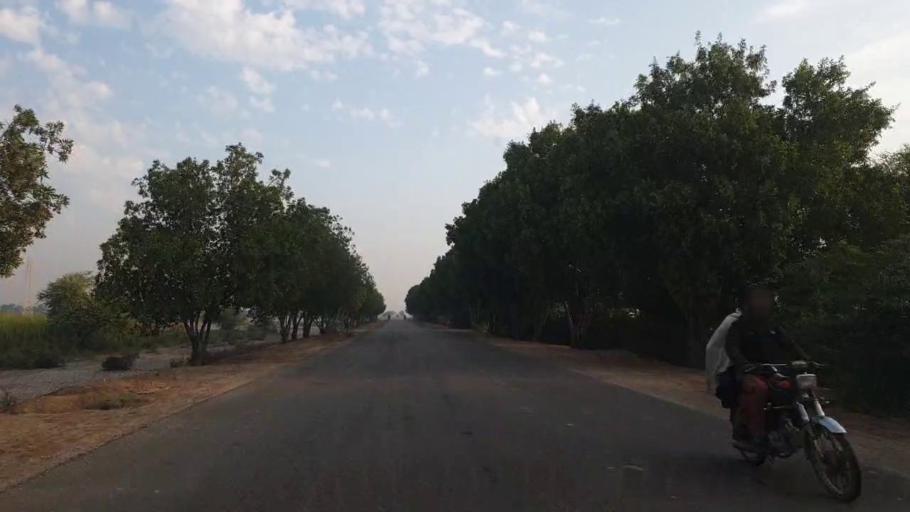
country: PK
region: Sindh
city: Badin
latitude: 24.6840
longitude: 68.9120
